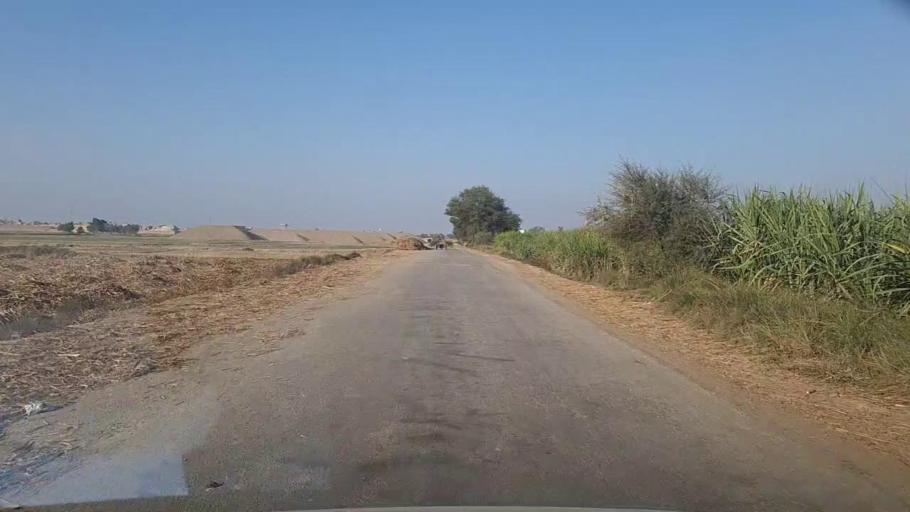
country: PK
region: Sindh
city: Phulji
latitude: 26.8534
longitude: 67.7937
